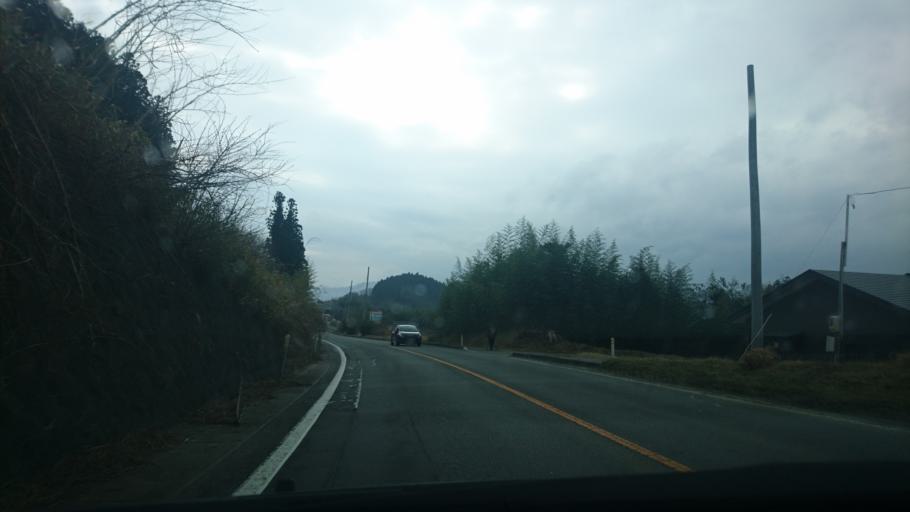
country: JP
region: Iwate
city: Ofunato
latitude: 39.0196
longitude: 141.6715
